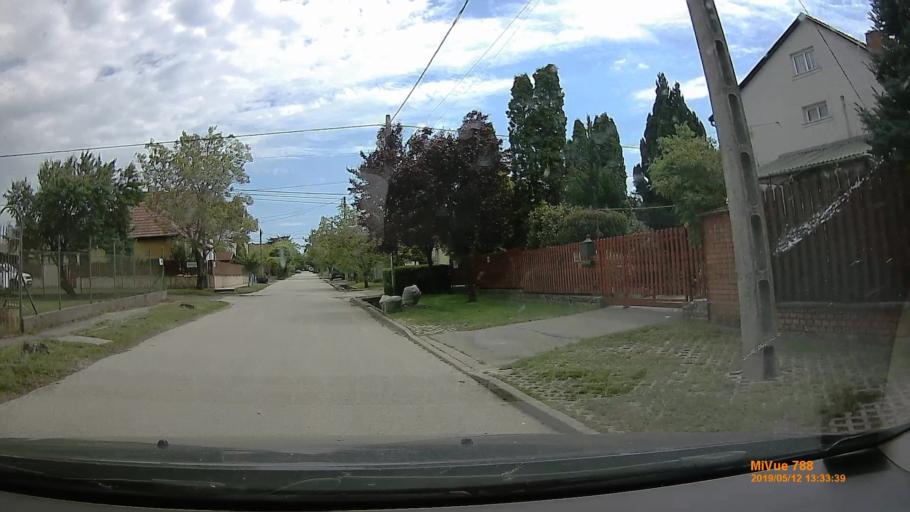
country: HU
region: Pest
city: Ecser
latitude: 47.4773
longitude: 19.2987
